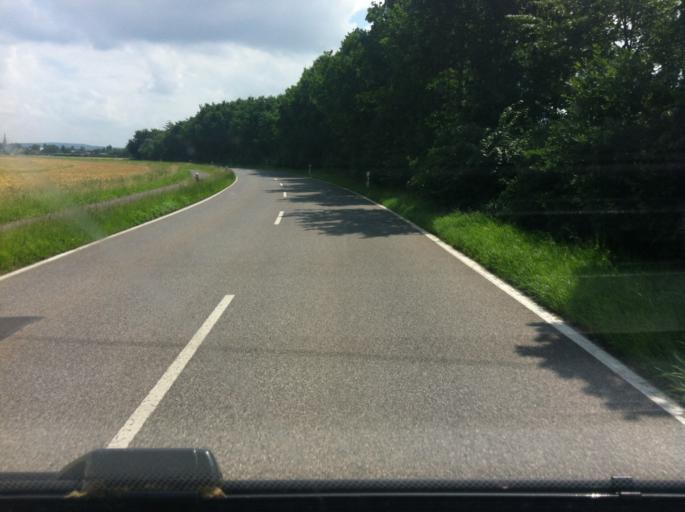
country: DE
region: North Rhine-Westphalia
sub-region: Regierungsbezirk Koln
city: Euskirchen
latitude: 50.6686
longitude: 6.8289
